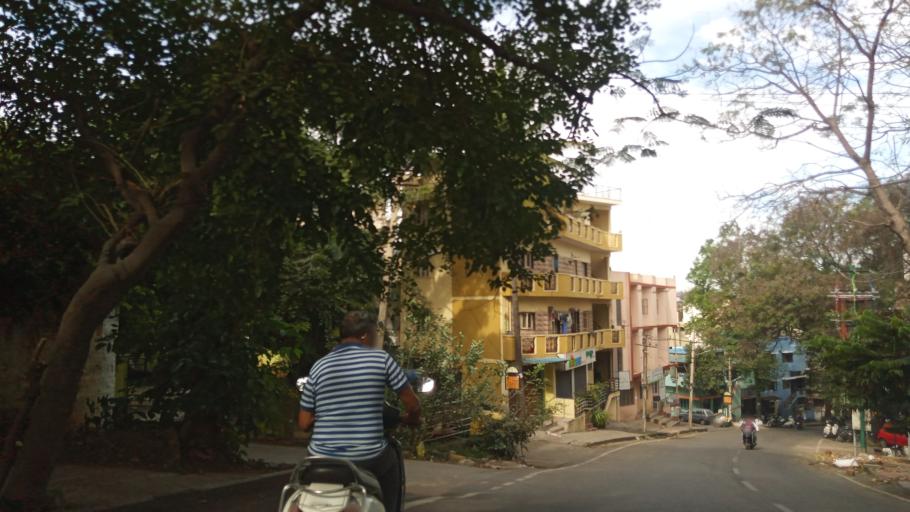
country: IN
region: Karnataka
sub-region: Bangalore Urban
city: Bangalore
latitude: 13.0109
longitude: 77.5459
